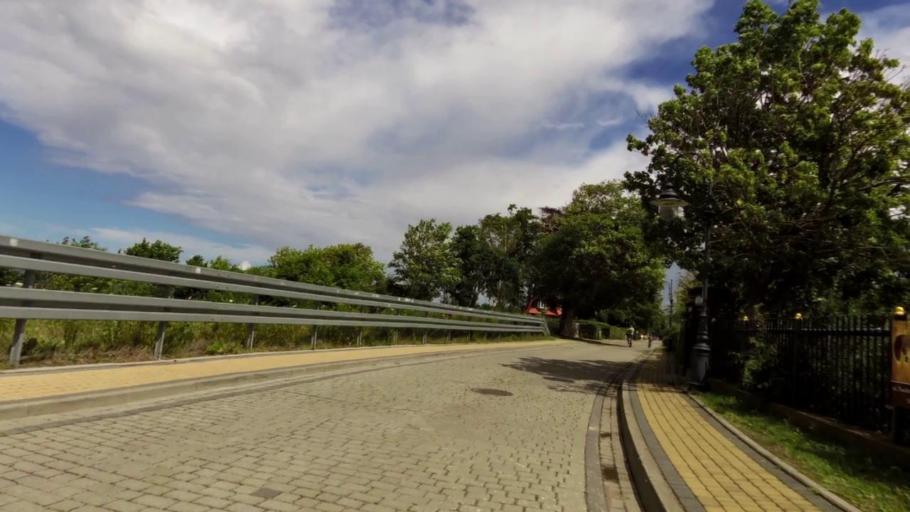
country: PL
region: West Pomeranian Voivodeship
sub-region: Powiat slawienski
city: Darlowo
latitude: 54.5391
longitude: 16.5286
